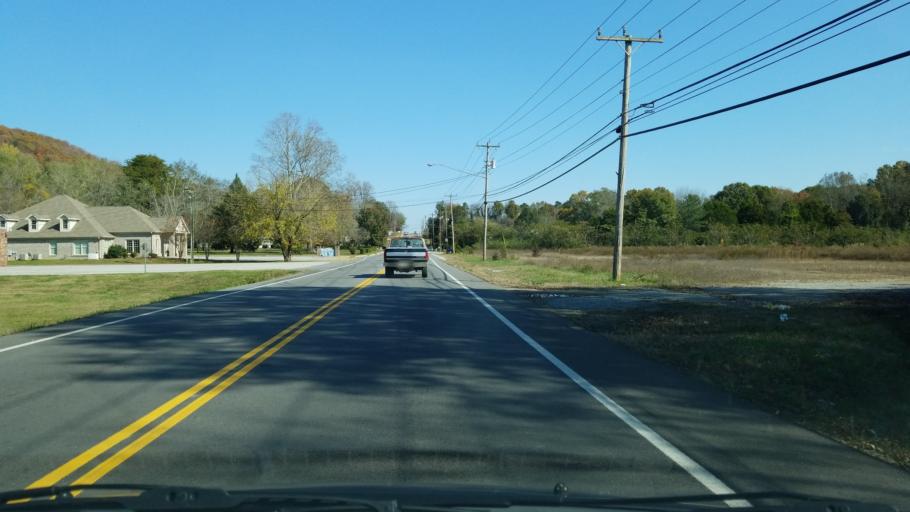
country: US
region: Tennessee
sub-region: Hamilton County
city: Soddy-Daisy
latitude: 35.2297
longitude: -85.2099
